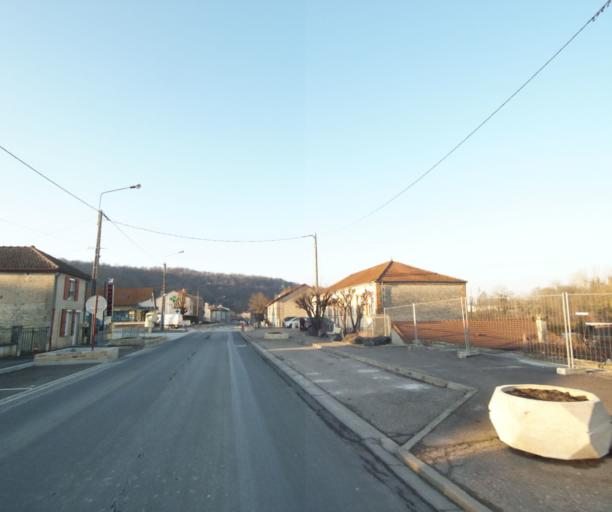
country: FR
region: Champagne-Ardenne
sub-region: Departement de la Haute-Marne
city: Chevillon
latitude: 48.5276
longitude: 5.0996
